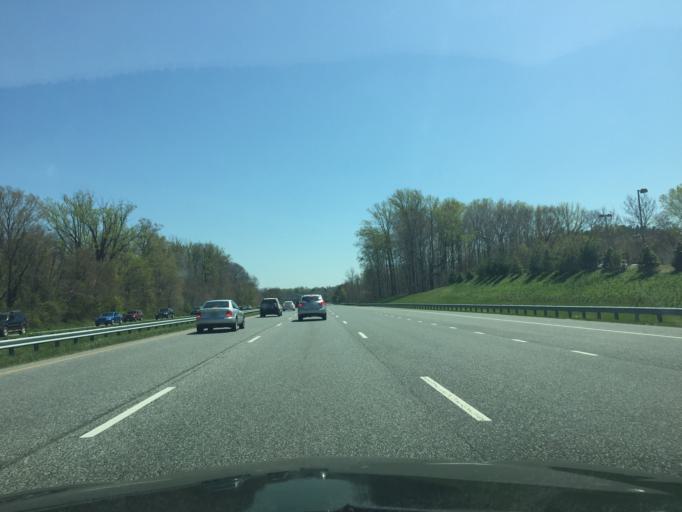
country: US
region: Maryland
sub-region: Harford County
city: South Bel Air
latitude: 39.5162
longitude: -76.3432
